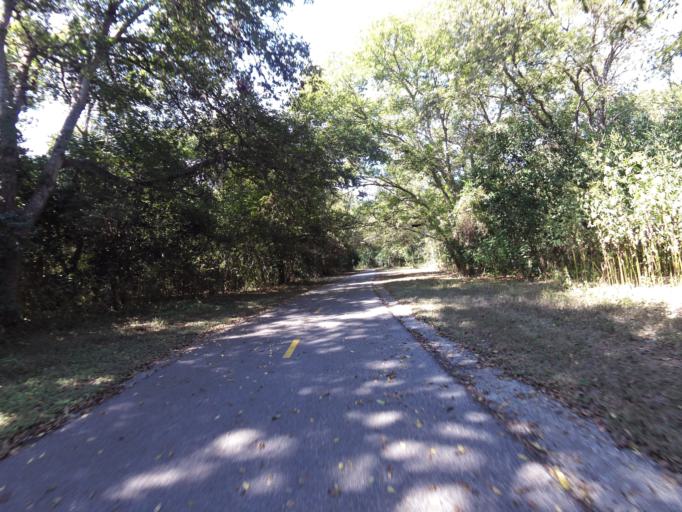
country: US
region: Texas
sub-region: Bexar County
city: Kirby
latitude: 29.4047
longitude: -98.4240
